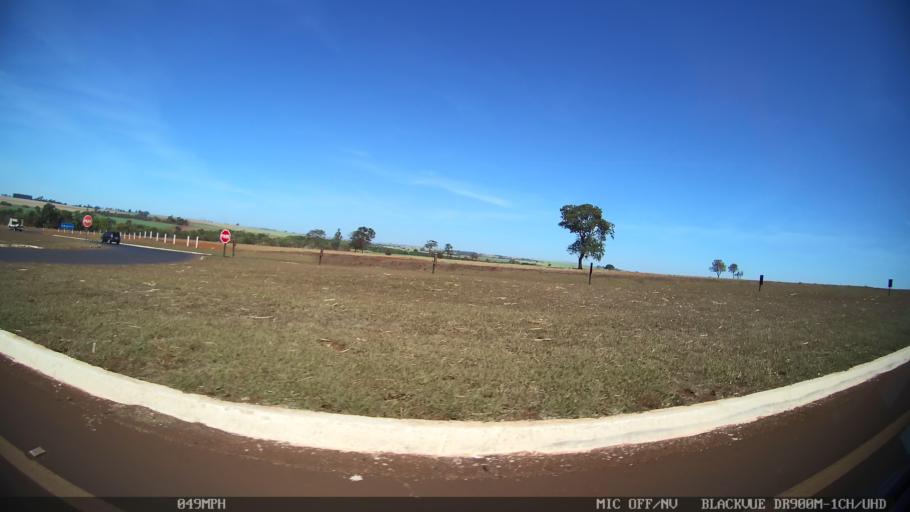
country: BR
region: Sao Paulo
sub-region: Sao Joaquim Da Barra
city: Sao Joaquim da Barra
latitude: -20.5126
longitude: -47.8989
